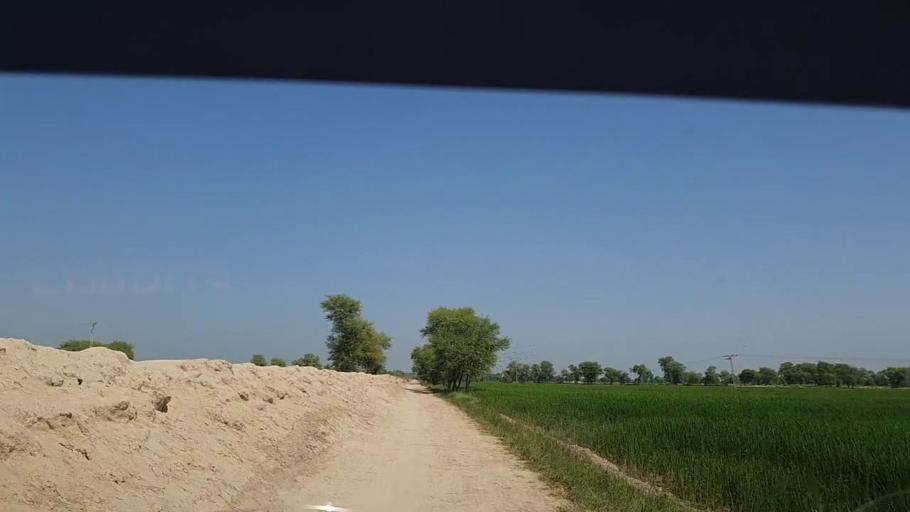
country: PK
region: Sindh
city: Tangwani
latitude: 28.2885
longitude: 69.0455
